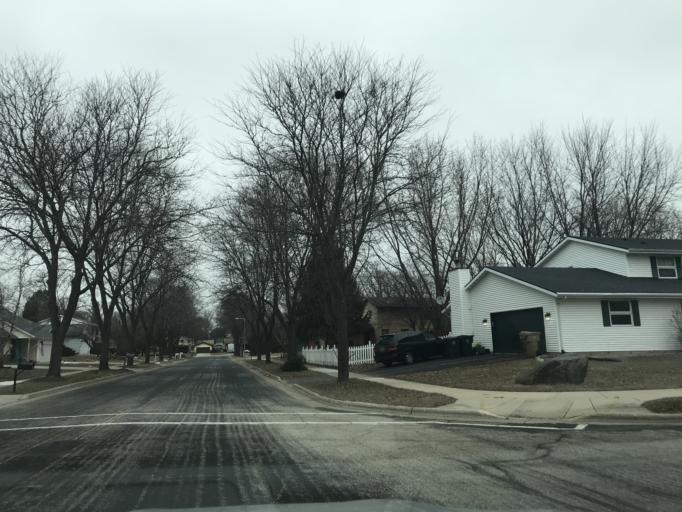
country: US
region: Wisconsin
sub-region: Dane County
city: Monona
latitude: 43.0971
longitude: -89.2958
